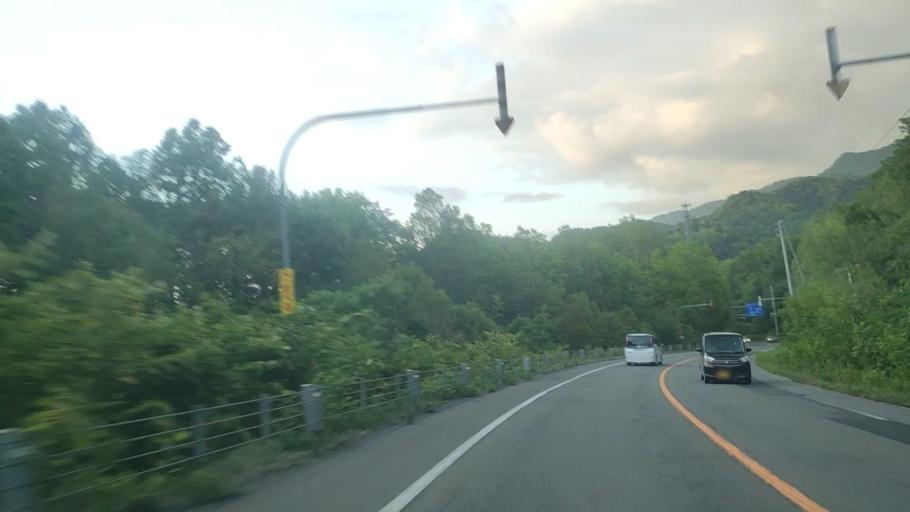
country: JP
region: Hokkaido
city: Ashibetsu
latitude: 43.3774
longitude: 142.1758
